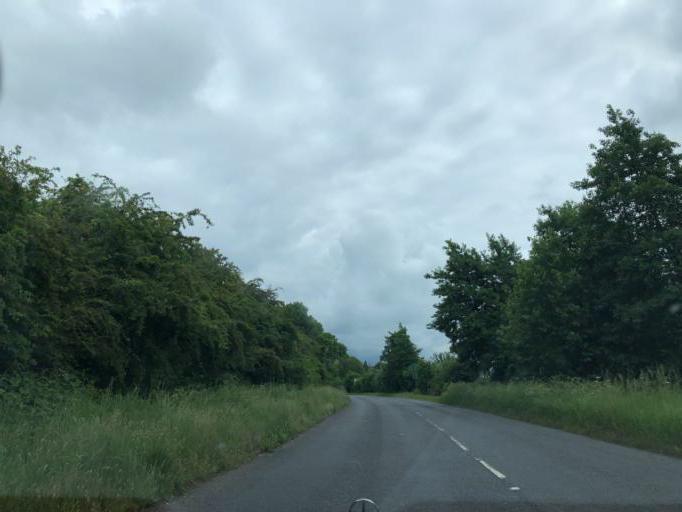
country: GB
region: England
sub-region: Solihull
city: Balsall Common
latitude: 52.3856
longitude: -1.6297
